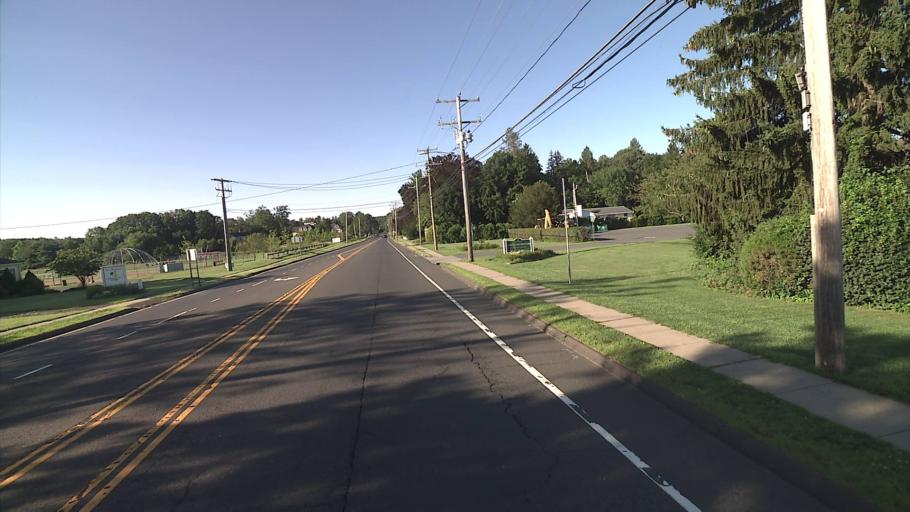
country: US
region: Connecticut
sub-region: New Haven County
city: Cheshire
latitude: 41.4887
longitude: -72.9049
